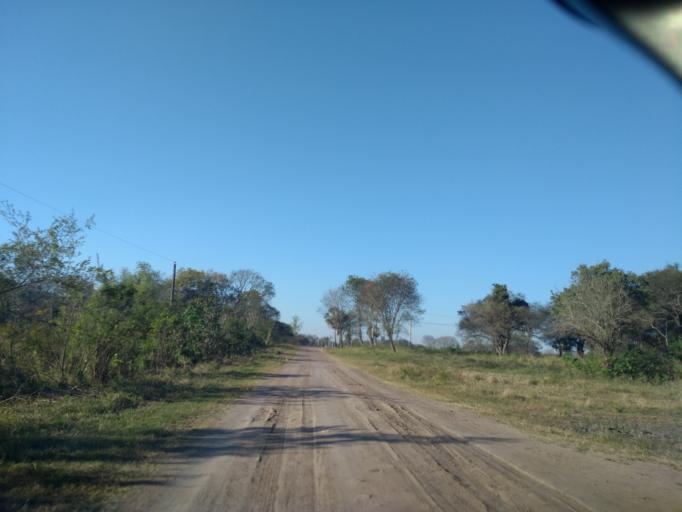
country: AR
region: Chaco
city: Barranqueras
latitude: -27.4369
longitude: -58.9280
